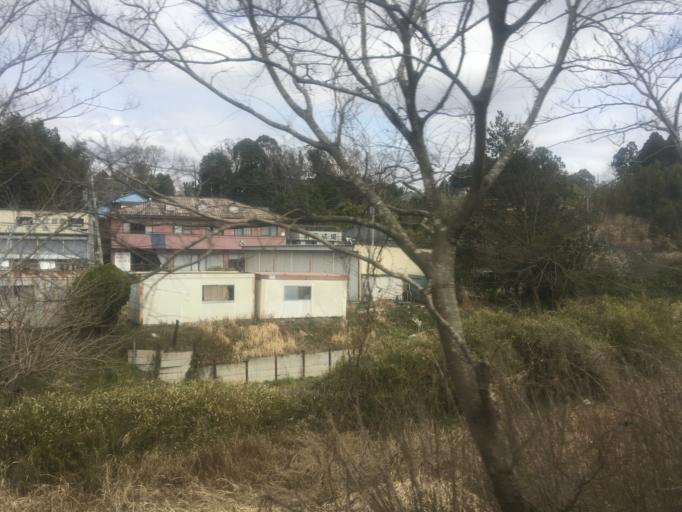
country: JP
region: Chiba
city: Yachimata
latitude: 35.6484
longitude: 140.3394
